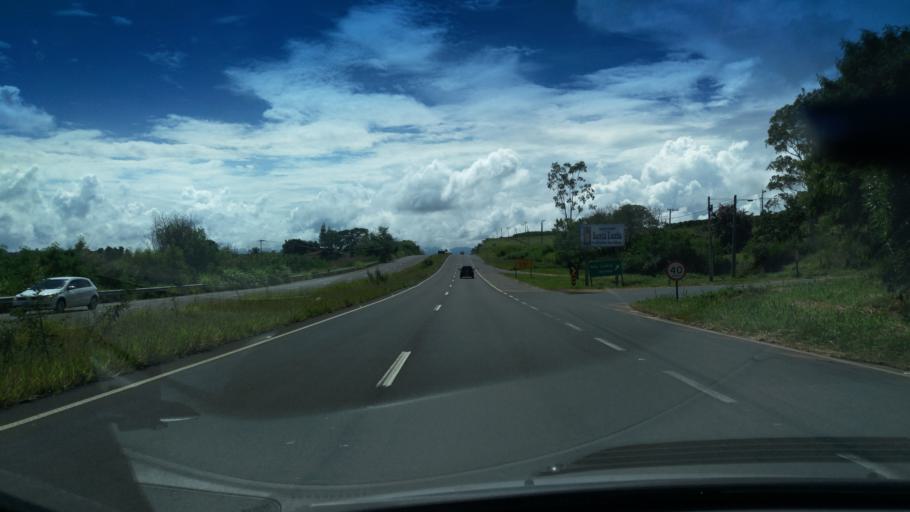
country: BR
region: Sao Paulo
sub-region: Santo Antonio Do Jardim
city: Espirito Santo do Pinhal
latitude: -22.1730
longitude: -46.7458
